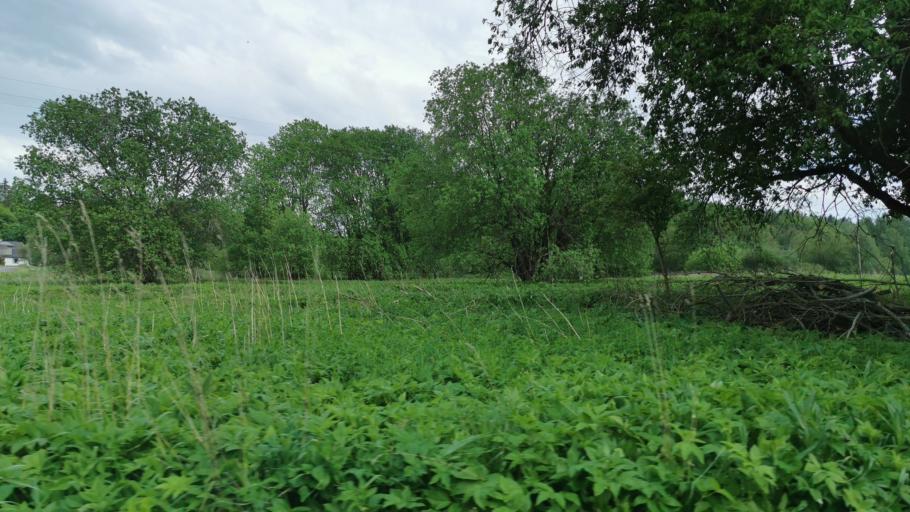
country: EE
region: Laeaene-Virumaa
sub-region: Rakvere linn
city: Rakvere
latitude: 59.2739
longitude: 26.3499
